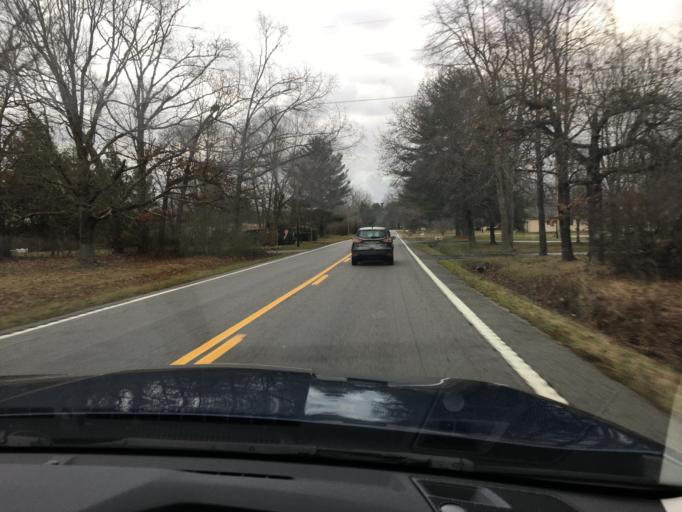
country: US
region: Tennessee
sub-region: Cumberland County
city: Crossville
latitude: 35.9080
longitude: -84.9670
